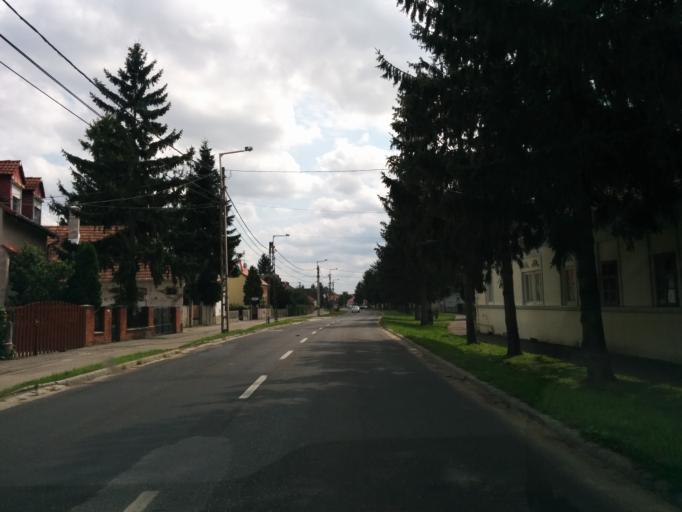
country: HU
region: Vas
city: Buk
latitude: 47.3791
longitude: 16.7592
